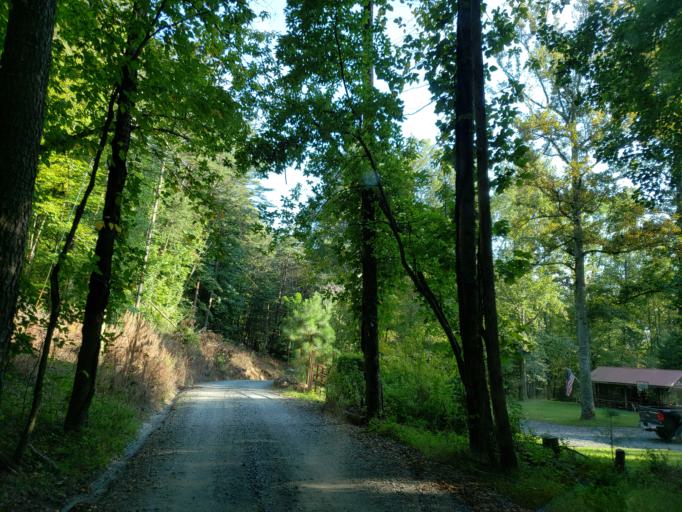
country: US
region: Georgia
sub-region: Fannin County
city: Blue Ridge
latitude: 34.6922
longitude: -84.2704
